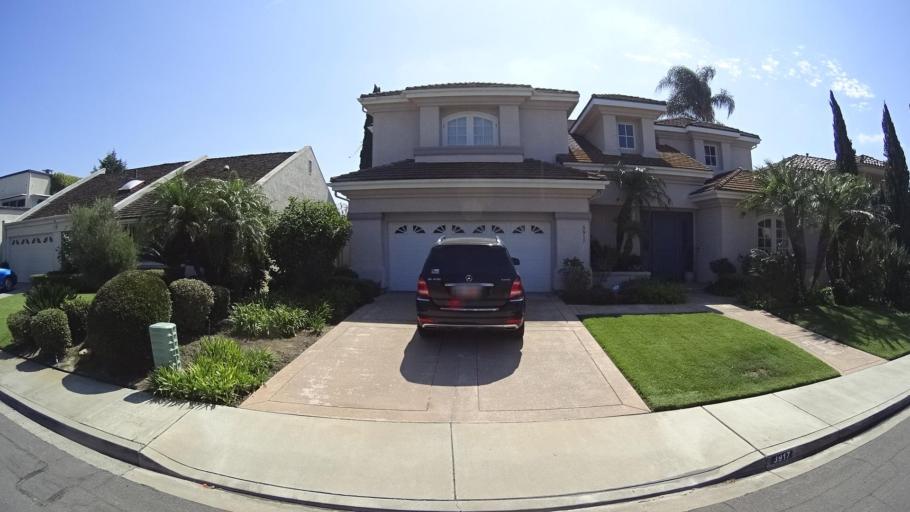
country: US
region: California
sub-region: San Diego County
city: Fairbanks Ranch
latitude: 32.9877
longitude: -117.2112
